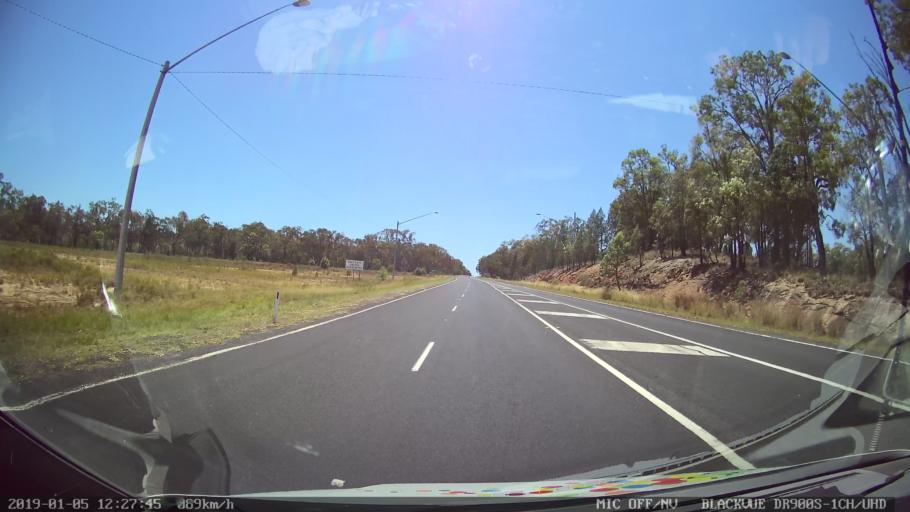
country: AU
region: New South Wales
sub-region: Warrumbungle Shire
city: Coonabarabran
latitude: -31.2454
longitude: 149.3138
